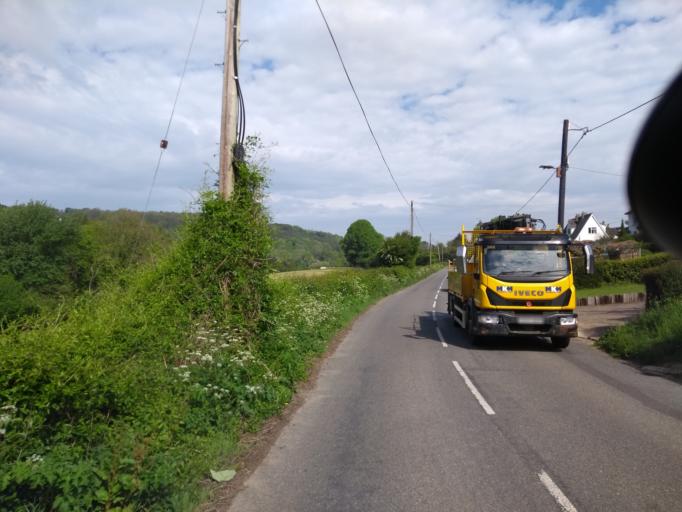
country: GB
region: England
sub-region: Dorset
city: Lyme Regis
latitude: 50.7396
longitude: -2.9641
